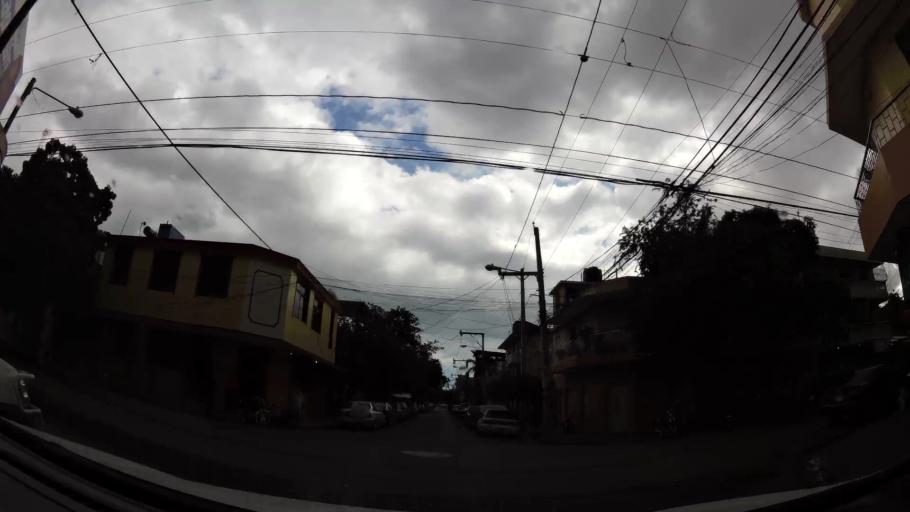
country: DO
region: Nacional
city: San Carlos
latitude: 18.4896
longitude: -69.9110
